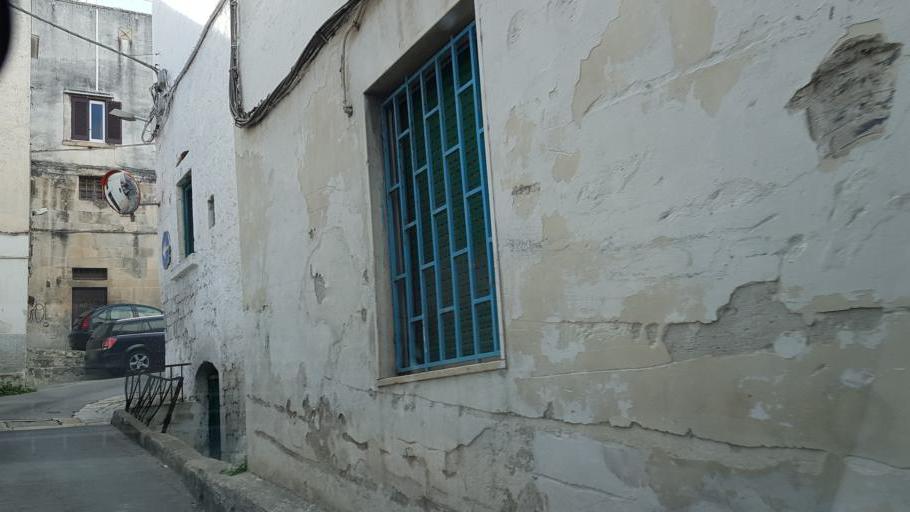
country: IT
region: Apulia
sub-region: Provincia di Brindisi
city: Ostuni
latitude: 40.7313
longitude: 17.5799
